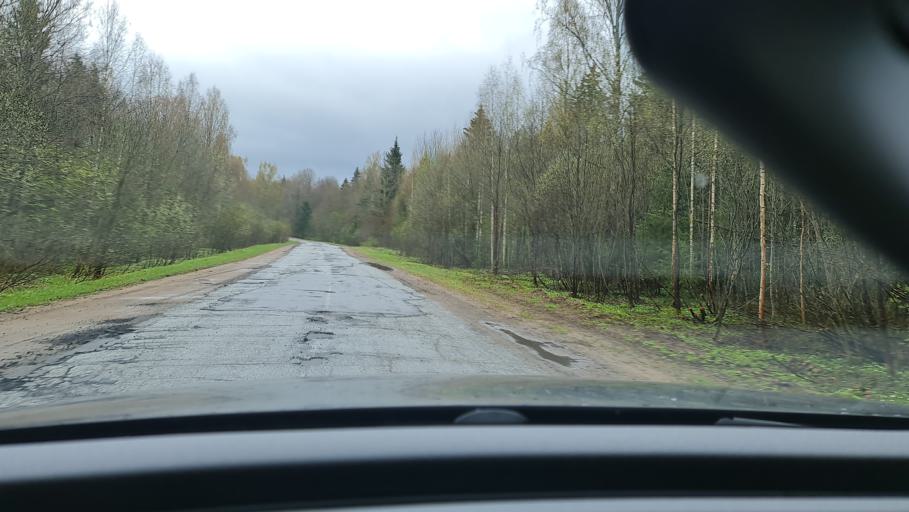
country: RU
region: Novgorod
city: Marevo
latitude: 57.2925
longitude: 32.0803
